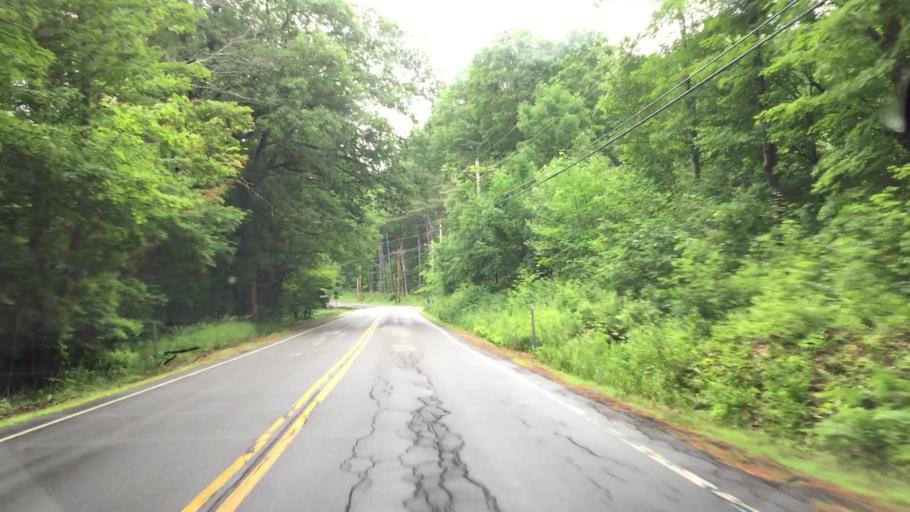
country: US
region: New Hampshire
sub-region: Carroll County
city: Center Harbor
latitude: 43.7563
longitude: -71.4823
